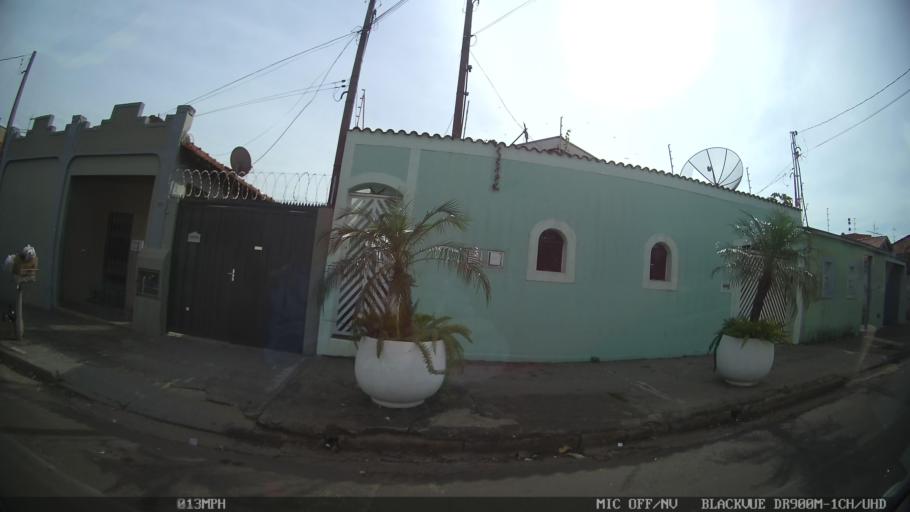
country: BR
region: Sao Paulo
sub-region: Piracicaba
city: Piracicaba
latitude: -22.7443
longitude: -47.6553
